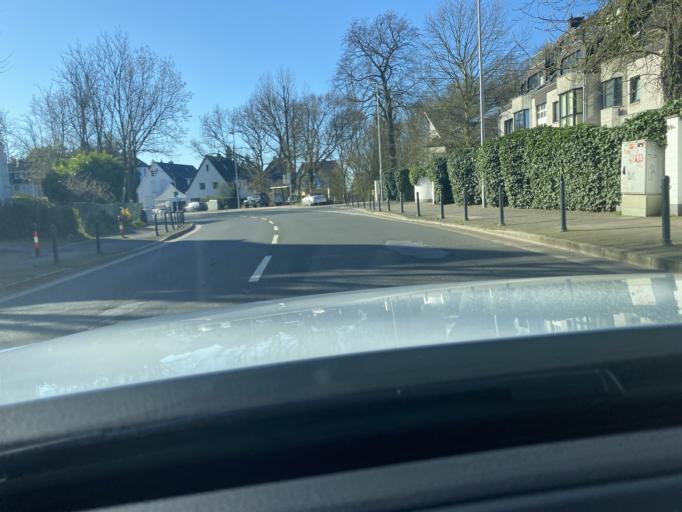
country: DE
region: North Rhine-Westphalia
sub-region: Regierungsbezirk Dusseldorf
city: Ratingen
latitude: 51.2493
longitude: 6.8602
